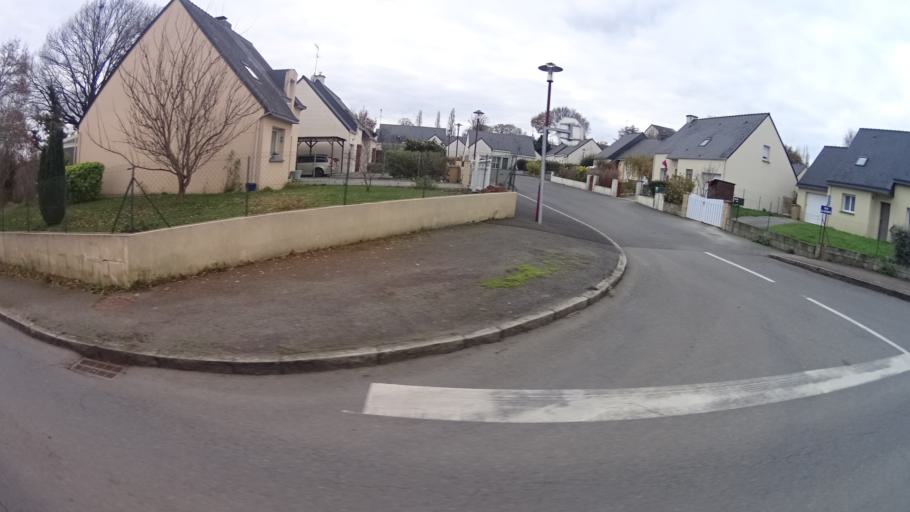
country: FR
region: Pays de la Loire
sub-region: Departement de la Loire-Atlantique
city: Avessac
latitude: 47.6536
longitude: -1.9856
